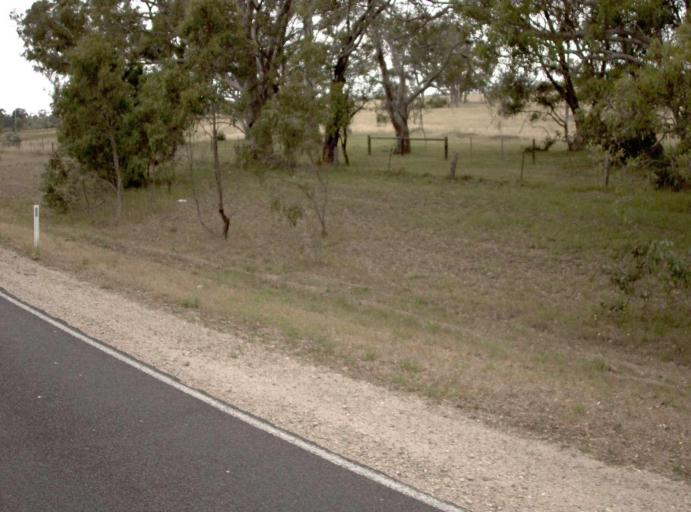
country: AU
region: Victoria
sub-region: Wellington
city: Sale
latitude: -38.1773
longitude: 147.1486
